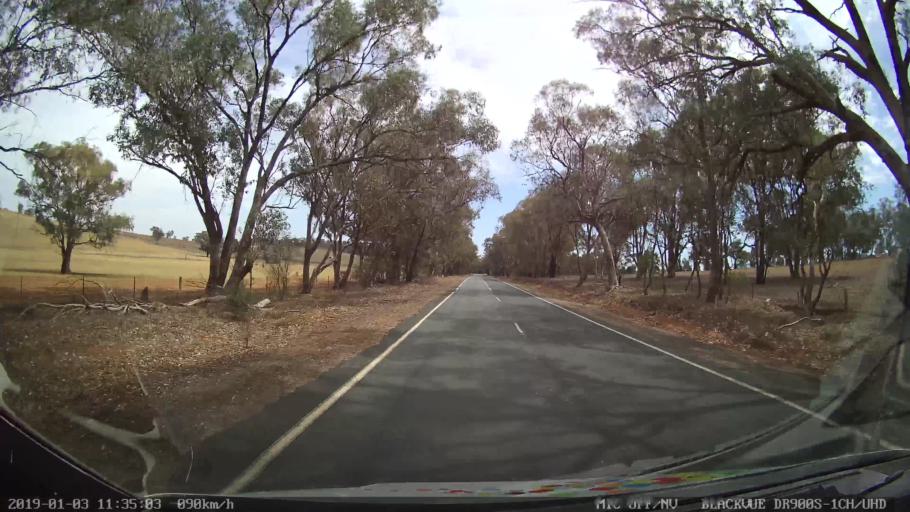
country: AU
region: New South Wales
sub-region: Weddin
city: Grenfell
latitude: -33.9272
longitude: 148.1600
